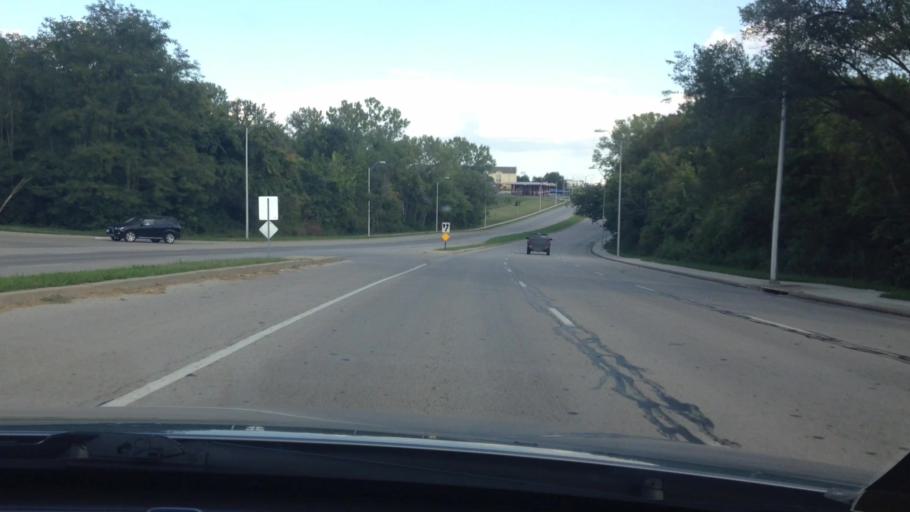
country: US
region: Missouri
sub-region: Clay County
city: Claycomo
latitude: 39.1703
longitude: -94.5018
